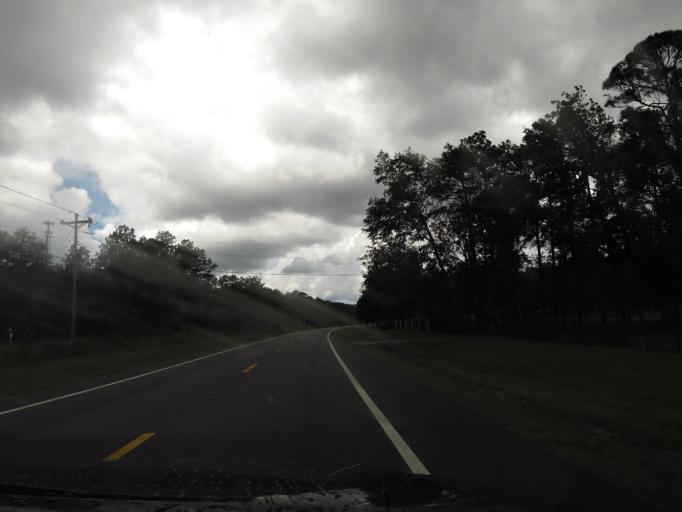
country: US
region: Florida
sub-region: Clay County
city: Asbury Lake
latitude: 30.0333
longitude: -81.8226
